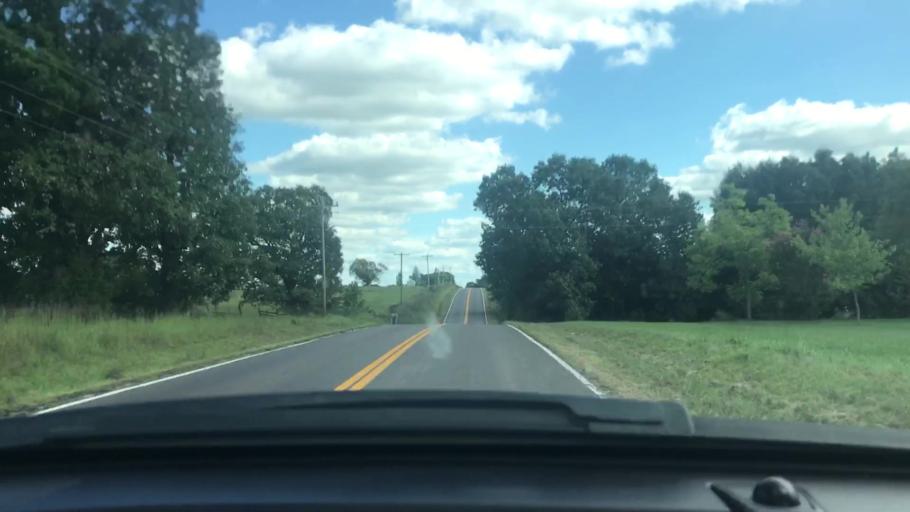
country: US
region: Missouri
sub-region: Wright County
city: Mountain Grove
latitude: 37.3109
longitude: -92.3169
